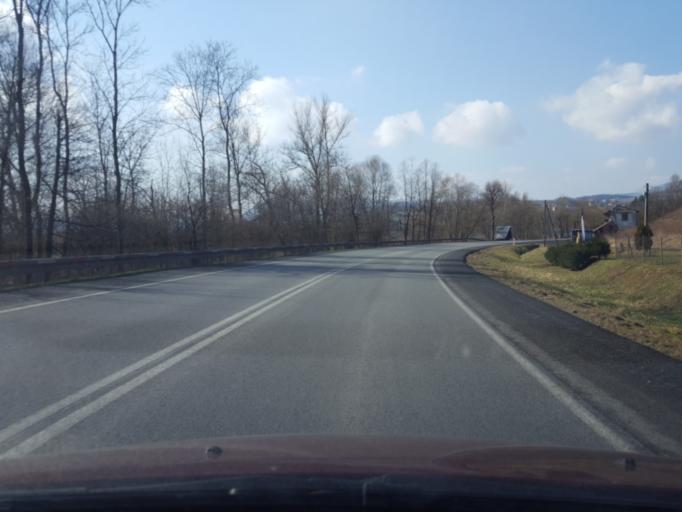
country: PL
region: Lesser Poland Voivodeship
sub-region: Powiat nowosadecki
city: Lososina Dolna
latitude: 49.7711
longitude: 20.6428
